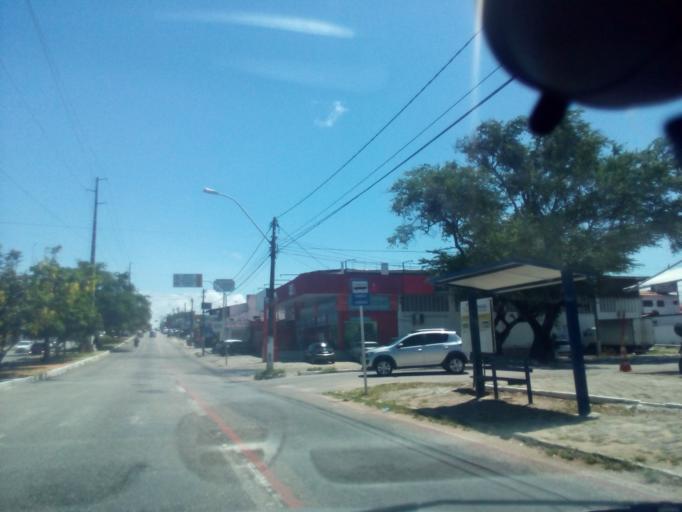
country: BR
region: Rio Grande do Norte
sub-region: Natal
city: Natal
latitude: -5.8322
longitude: -35.2177
